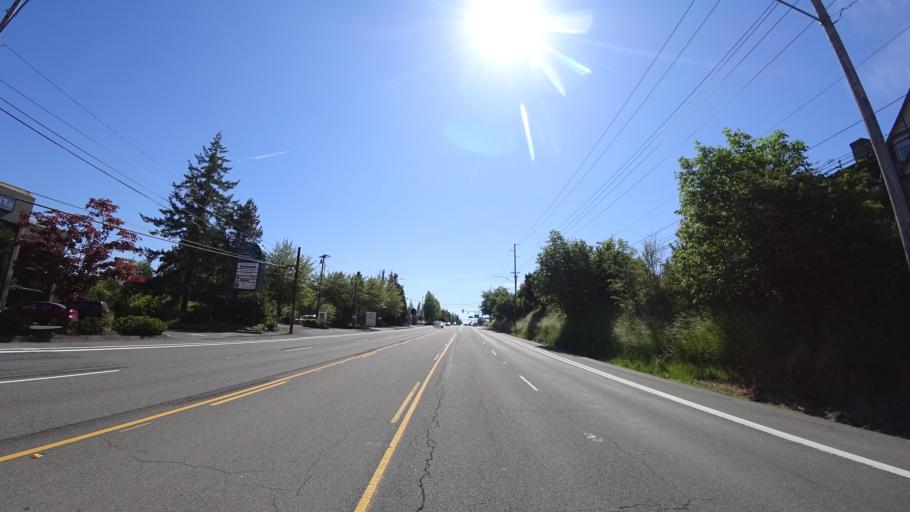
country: US
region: Oregon
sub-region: Washington County
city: Garden Home-Whitford
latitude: 45.4560
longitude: -122.7149
